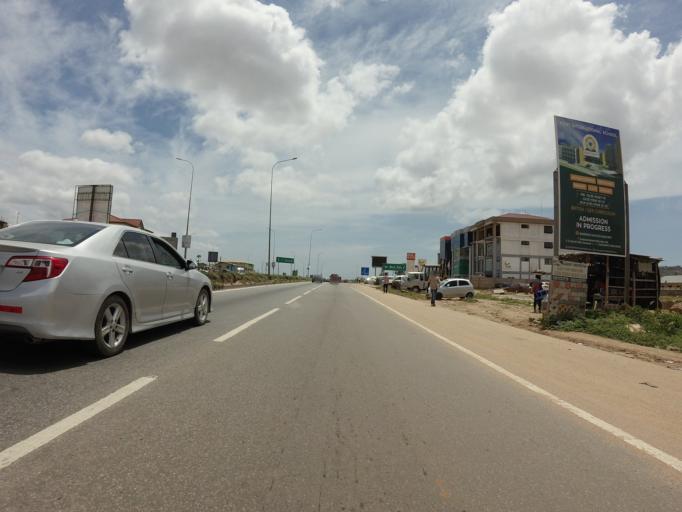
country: GH
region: Greater Accra
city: Gbawe
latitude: 5.5473
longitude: -0.3476
